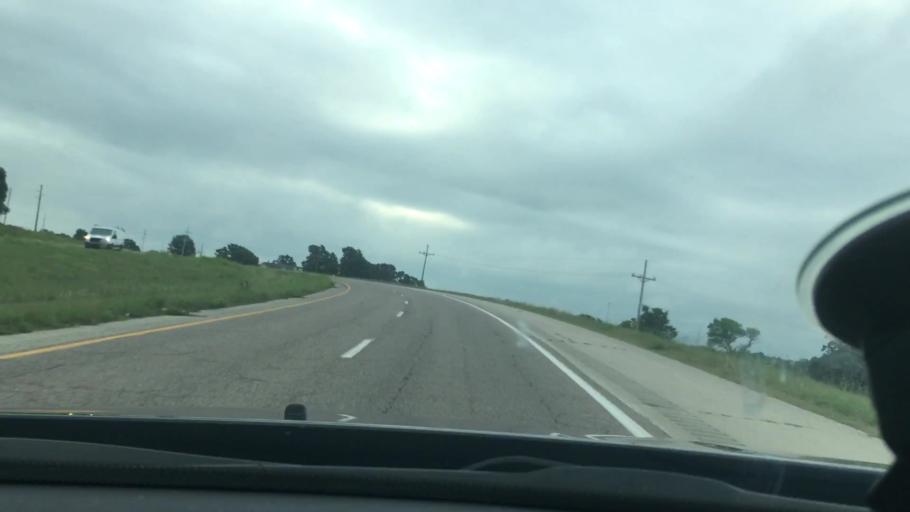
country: US
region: Oklahoma
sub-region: Pontotoc County
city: Ada
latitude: 34.7787
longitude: -96.5978
